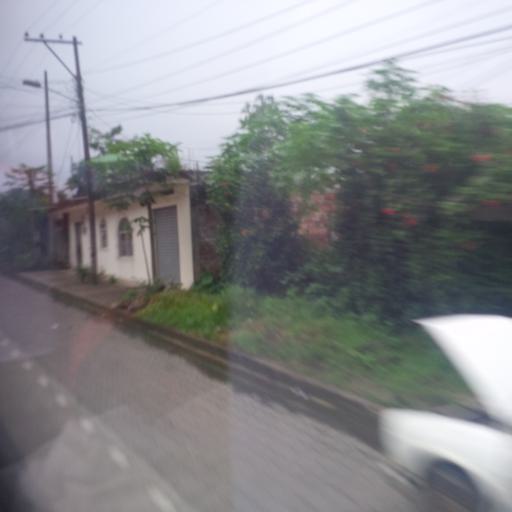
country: EC
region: Chimborazo
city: Alausi
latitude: -2.2018
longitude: -79.1247
